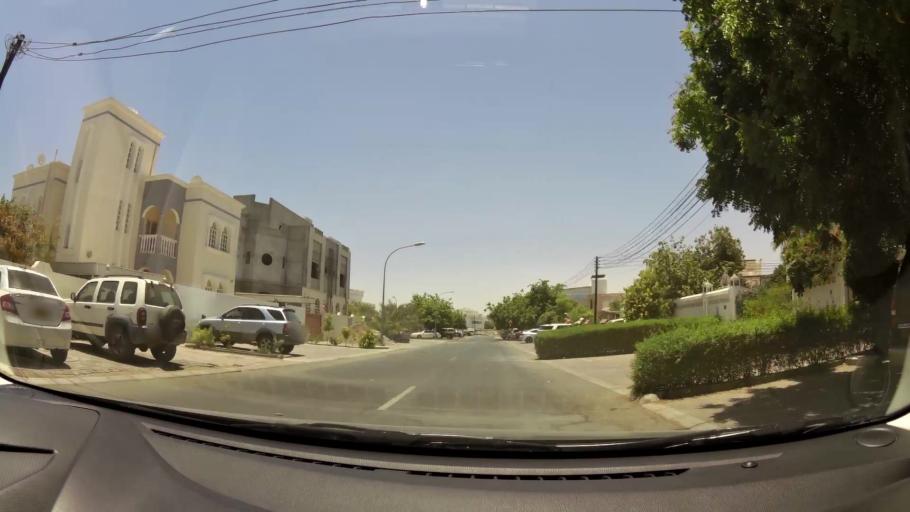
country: OM
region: Muhafazat Masqat
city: As Sib al Jadidah
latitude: 23.6342
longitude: 58.2333
